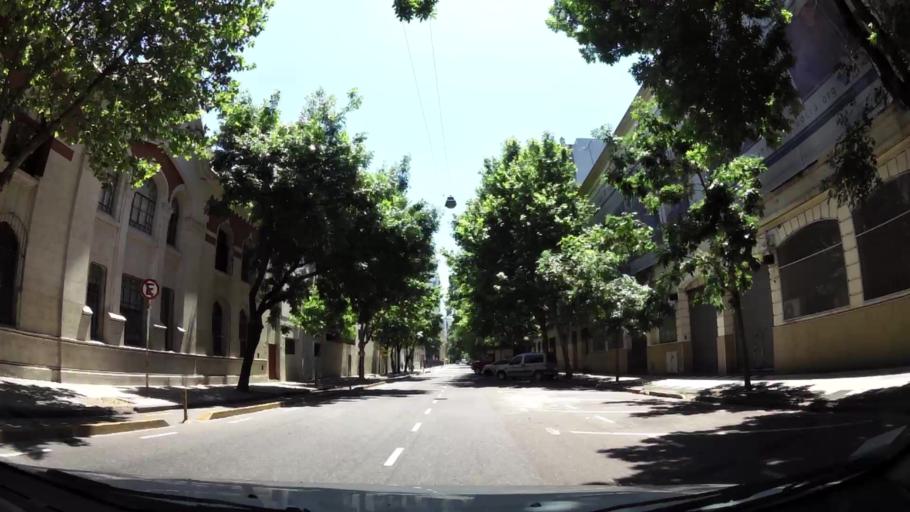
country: AR
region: Buenos Aires F.D.
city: Buenos Aires
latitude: -34.6191
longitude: -58.3672
